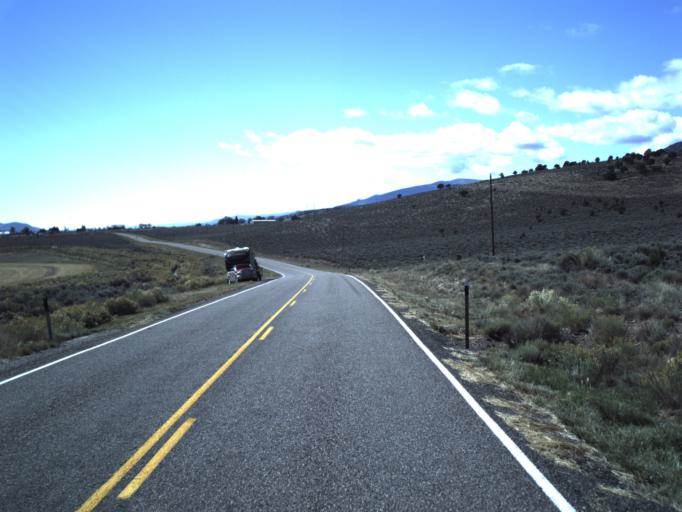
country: US
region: Utah
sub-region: Sevier County
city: Monroe
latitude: 38.5324
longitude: -111.8778
